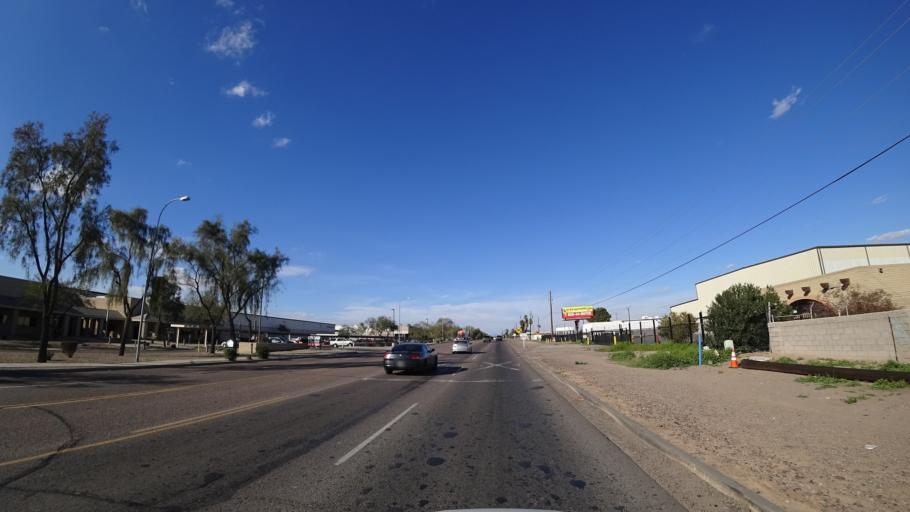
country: US
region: Arizona
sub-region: Maricopa County
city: Tolleson
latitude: 33.4418
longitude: -112.2382
